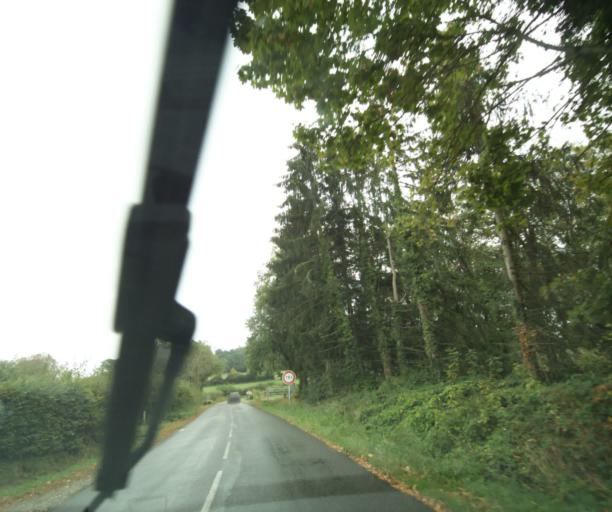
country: FR
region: Auvergne
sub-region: Departement du Puy-de-Dome
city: Durtol
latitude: 45.7970
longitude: 3.0326
